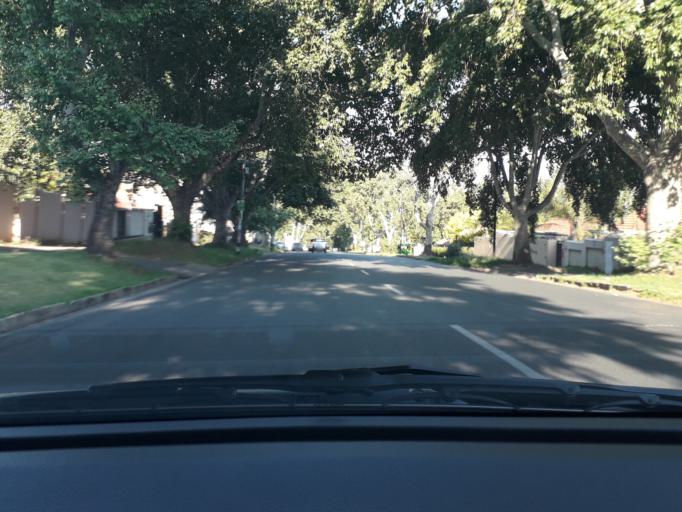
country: ZA
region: Gauteng
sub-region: City of Johannesburg Metropolitan Municipality
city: Johannesburg
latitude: -26.1791
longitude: 28.0978
